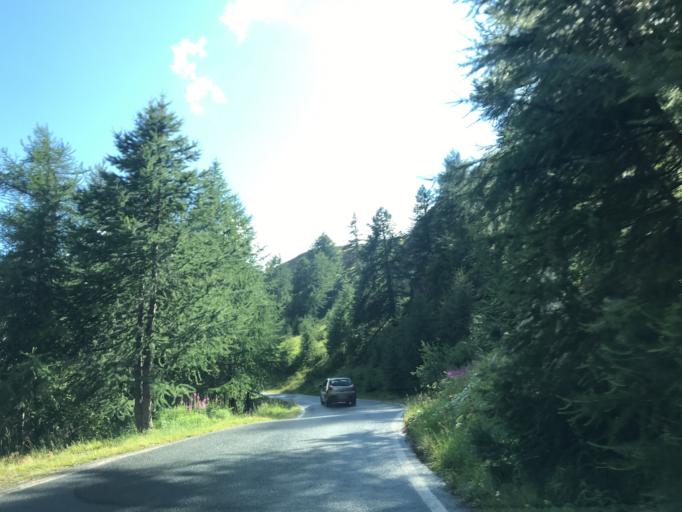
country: IT
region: Piedmont
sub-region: Provincia di Cuneo
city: Pontechianale
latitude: 44.6600
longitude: 6.9876
